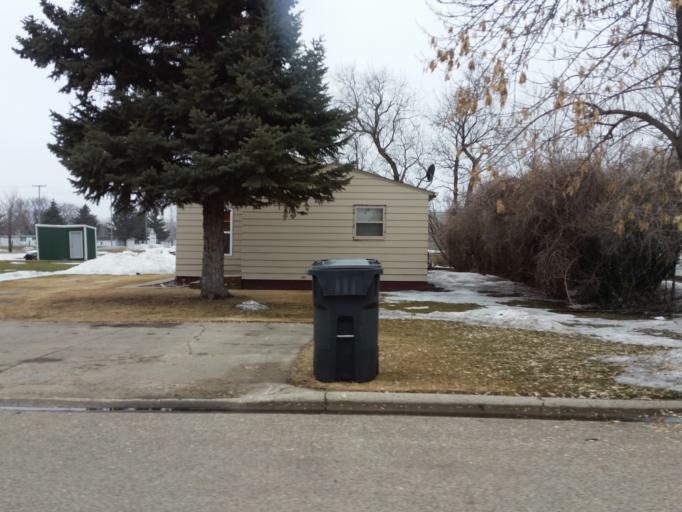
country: US
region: North Dakota
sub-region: Walsh County
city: Grafton
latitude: 48.6165
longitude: -97.4449
